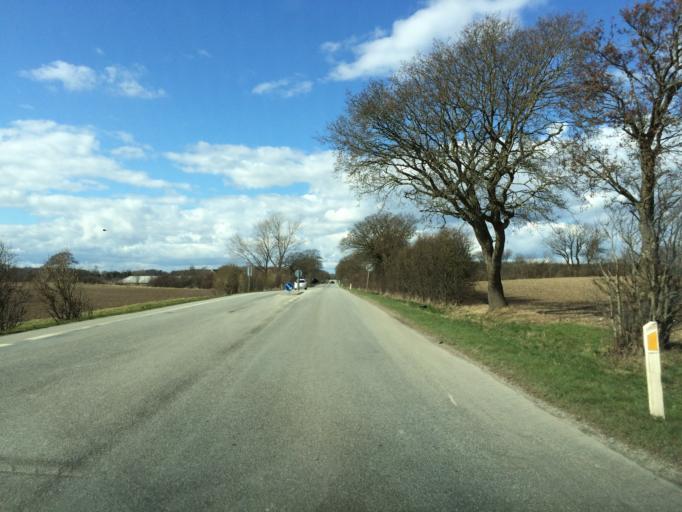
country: DK
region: South Denmark
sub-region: Middelfart Kommune
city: Brenderup
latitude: 55.4393
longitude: 9.9968
